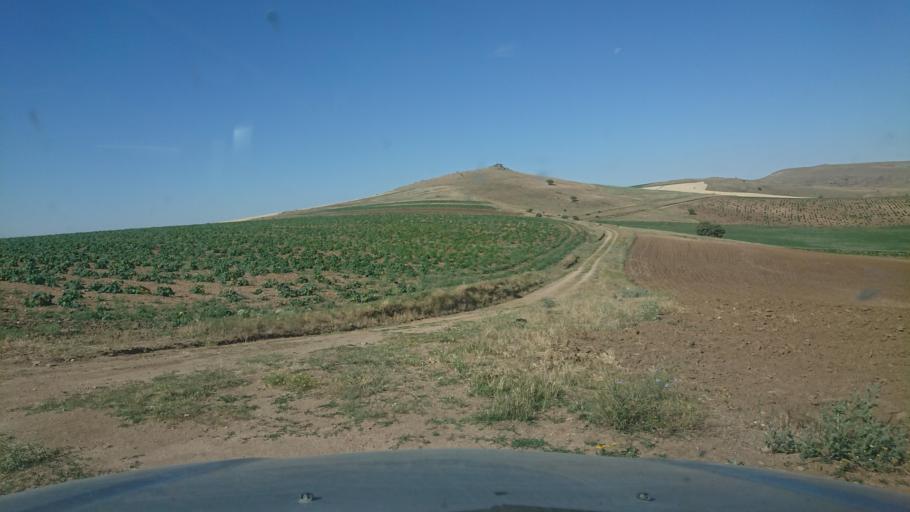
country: TR
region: Aksaray
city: Agacoren
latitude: 38.8372
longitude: 33.9375
